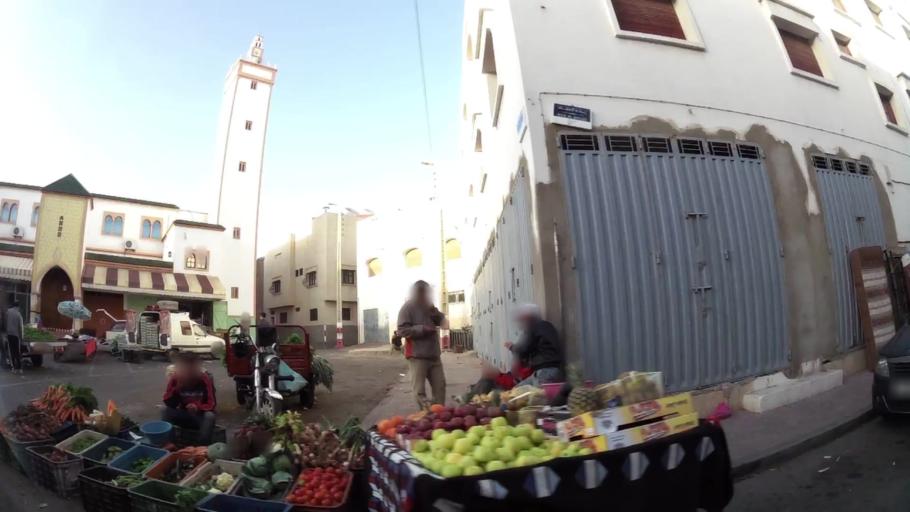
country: MA
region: Oued ed Dahab-Lagouira
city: Dakhla
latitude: 30.4141
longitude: -9.5590
